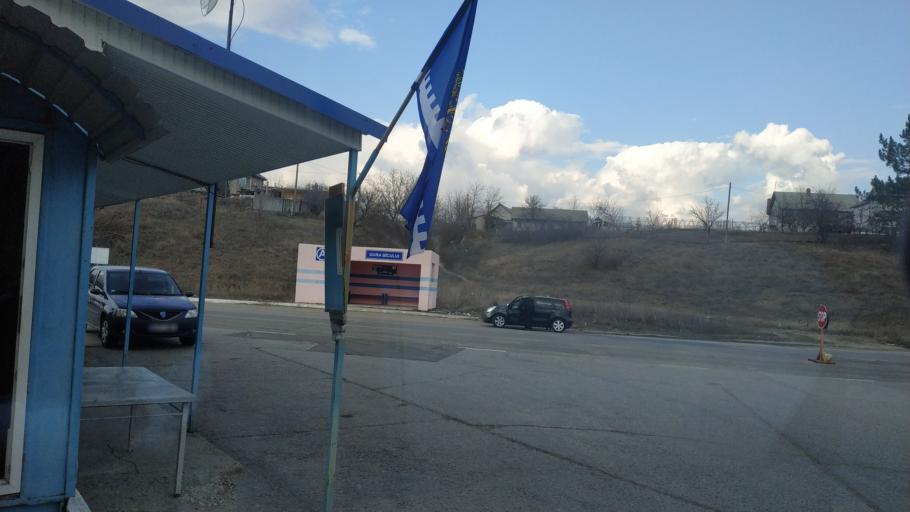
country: MD
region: Anenii Noi
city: Varnita
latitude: 46.9207
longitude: 29.4551
